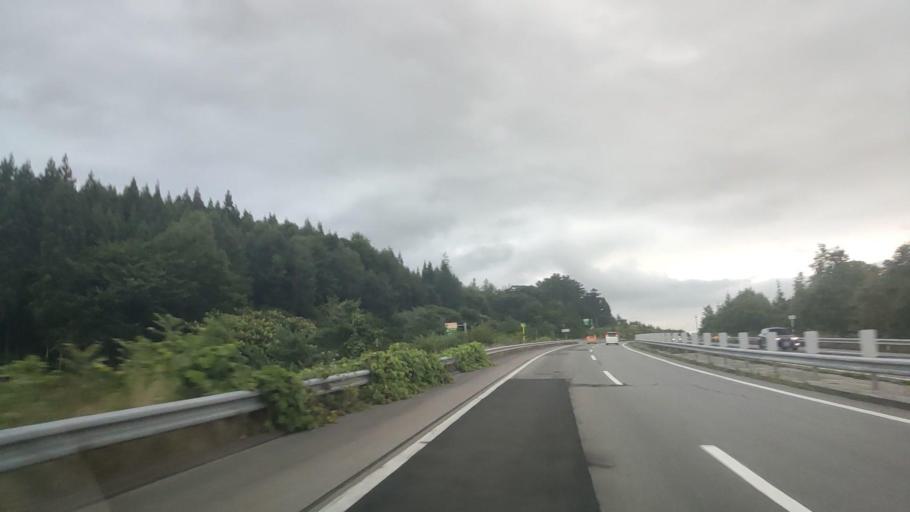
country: JP
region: Hokkaido
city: Nanae
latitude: 41.8985
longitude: 140.7065
